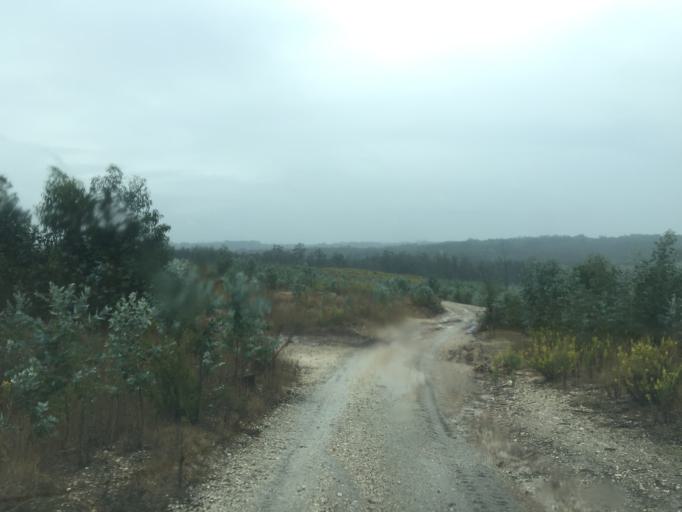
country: PT
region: Coimbra
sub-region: Figueira da Foz
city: Lavos
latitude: 40.0738
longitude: -8.7871
